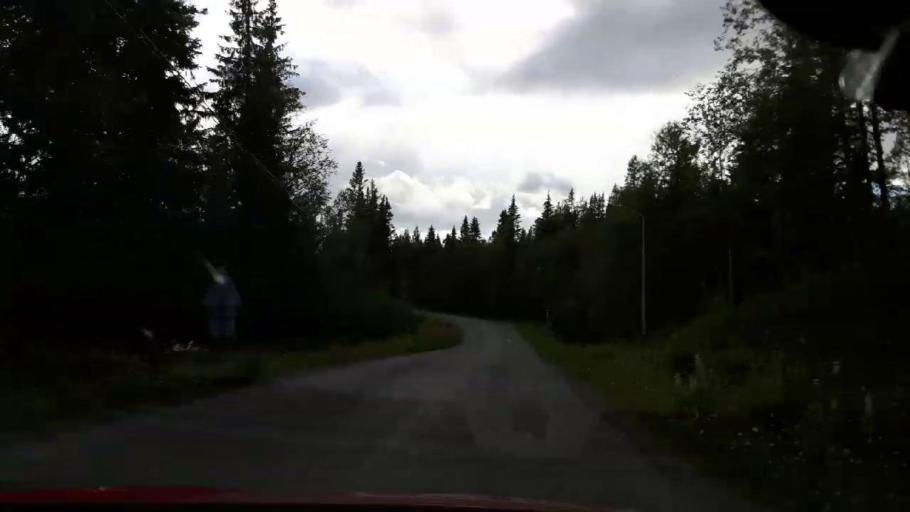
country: SE
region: Jaemtland
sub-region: Are Kommun
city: Are
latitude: 63.1647
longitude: 13.0573
